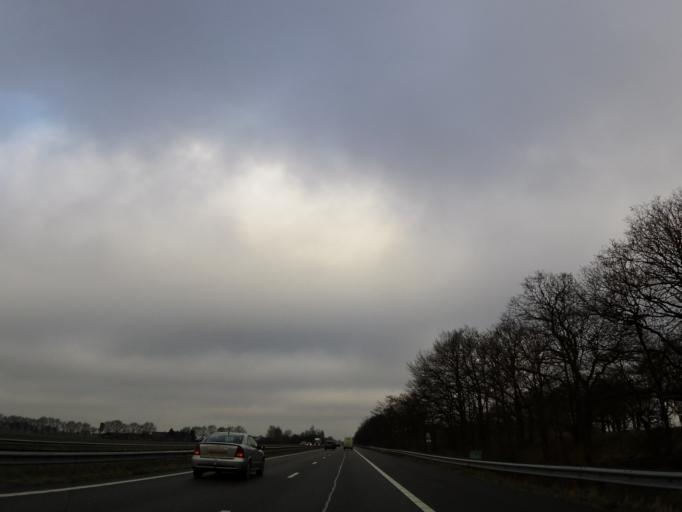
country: NL
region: Limburg
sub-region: Gemeente Leudal
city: Kelpen-Oler
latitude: 51.2074
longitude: 5.8229
